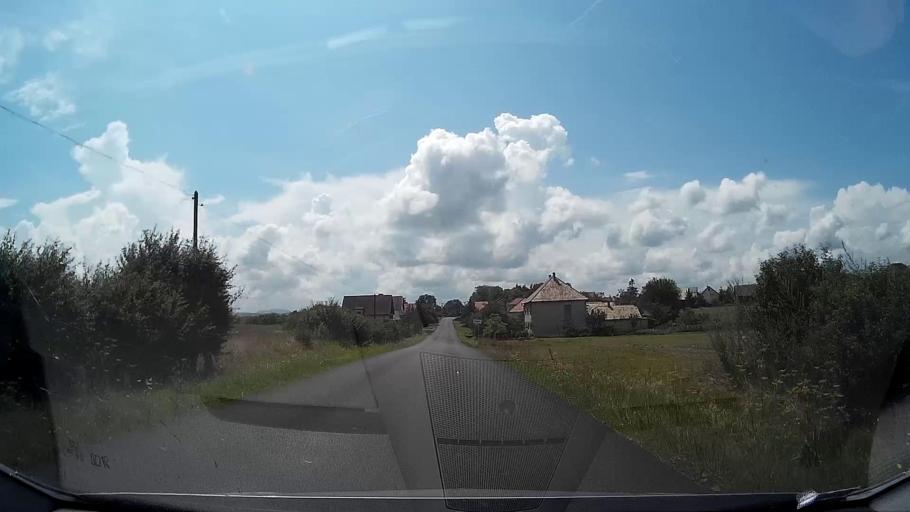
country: SK
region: Banskobystricky
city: Fil'akovo
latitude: 48.3109
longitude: 19.8038
